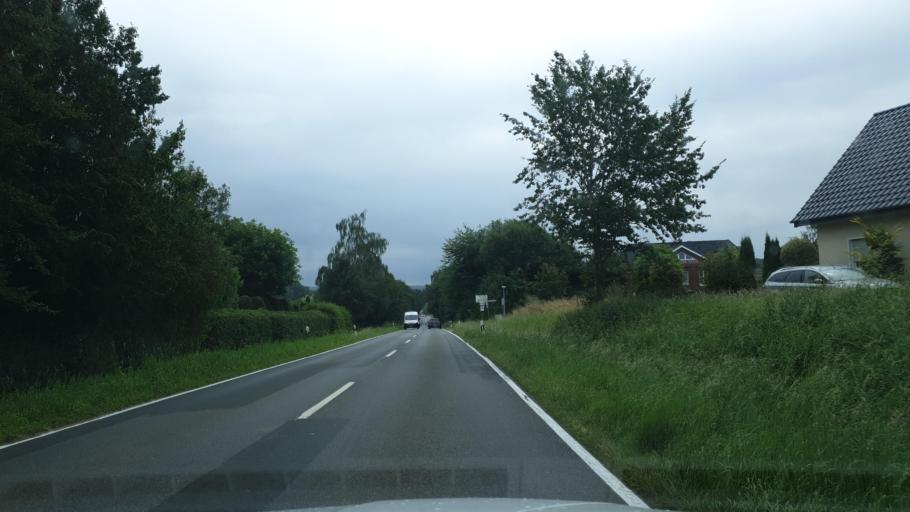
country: DE
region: North Rhine-Westphalia
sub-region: Regierungsbezirk Detmold
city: Bad Salzuflen
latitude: 52.1351
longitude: 8.7778
